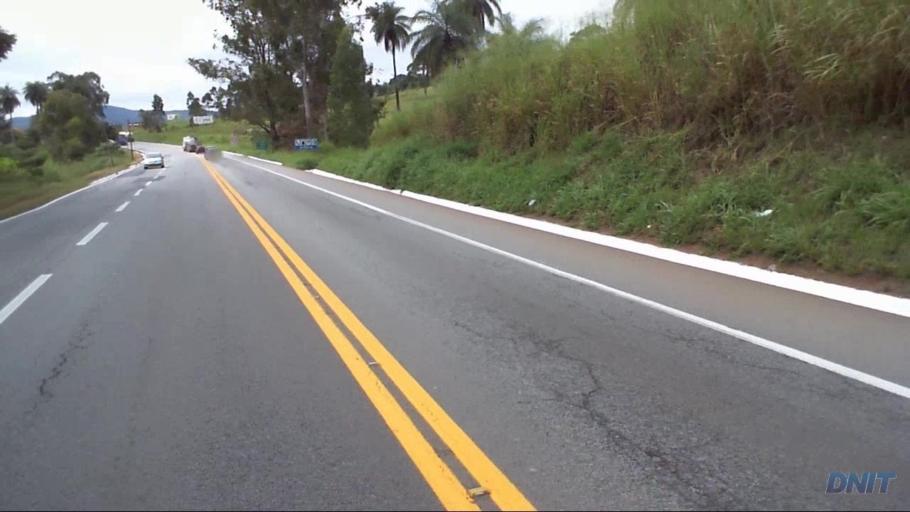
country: BR
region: Minas Gerais
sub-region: Caete
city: Caete
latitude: -19.7262
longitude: -43.5893
